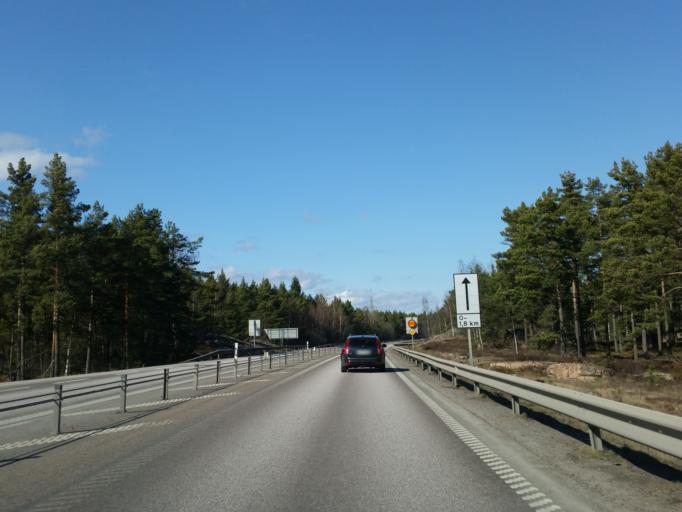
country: SE
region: Kalmar
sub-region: Oskarshamns Kommun
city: Oskarshamn
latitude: 57.2485
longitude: 16.4241
